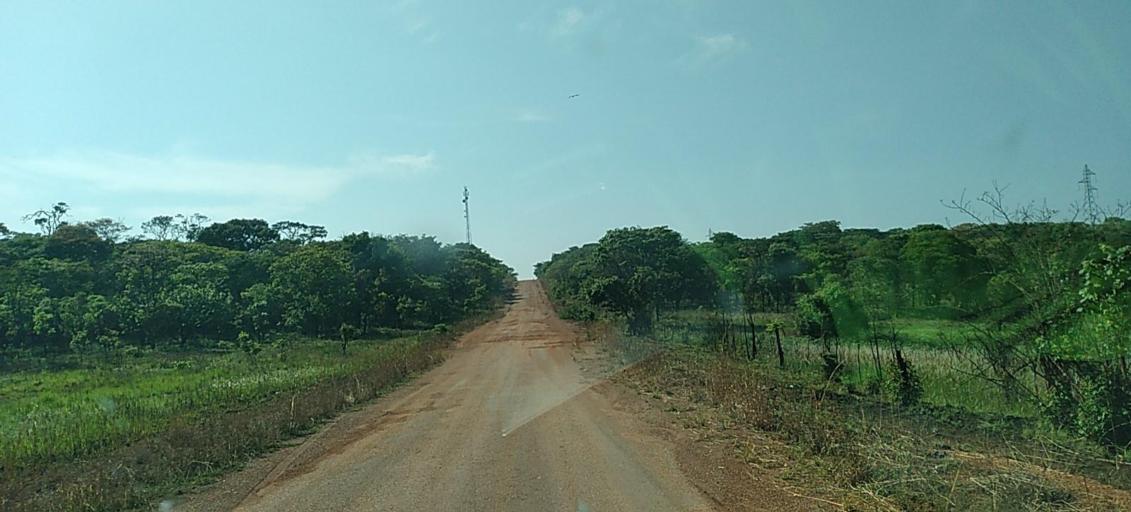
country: ZM
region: North-Western
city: Mwinilunga
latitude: -11.8071
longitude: 25.0814
